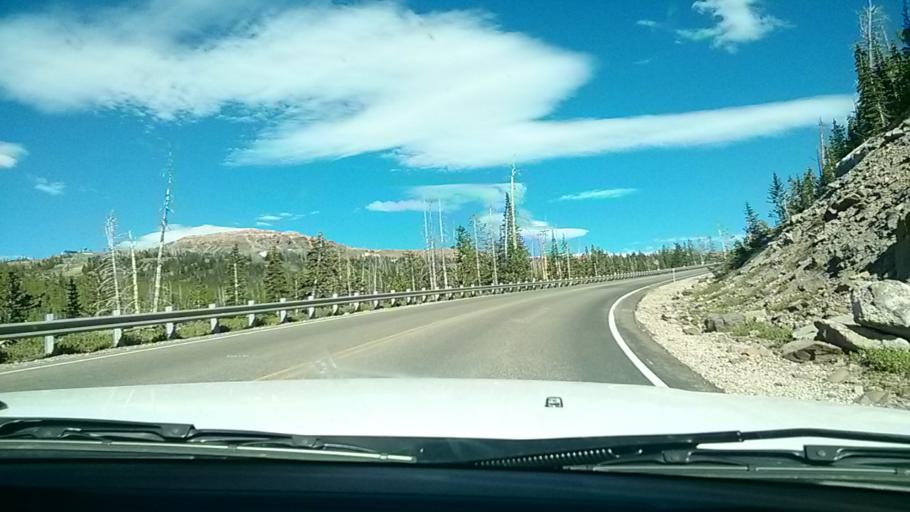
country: US
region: Utah
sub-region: Iron County
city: Parowan
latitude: 37.6810
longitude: -112.8524
